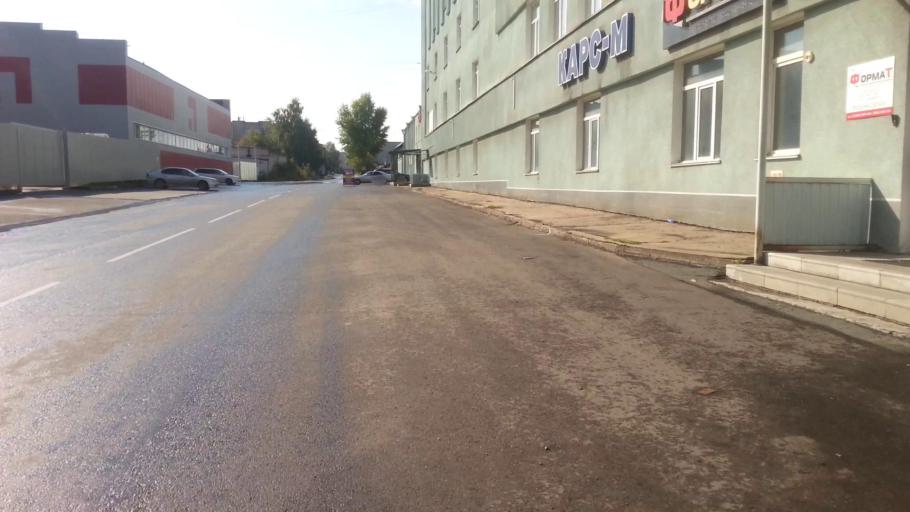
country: RU
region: Altai Krai
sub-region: Gorod Barnaulskiy
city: Barnaul
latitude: 53.3445
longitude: 83.7224
